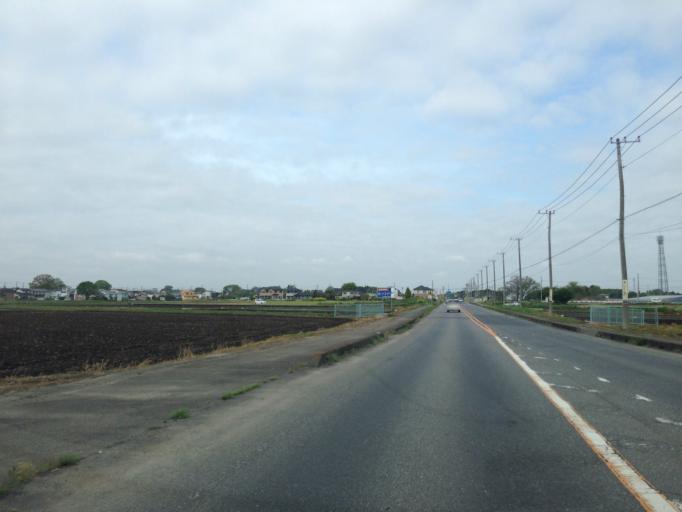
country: JP
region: Ibaraki
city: Ishige
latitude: 36.1477
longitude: 140.0223
